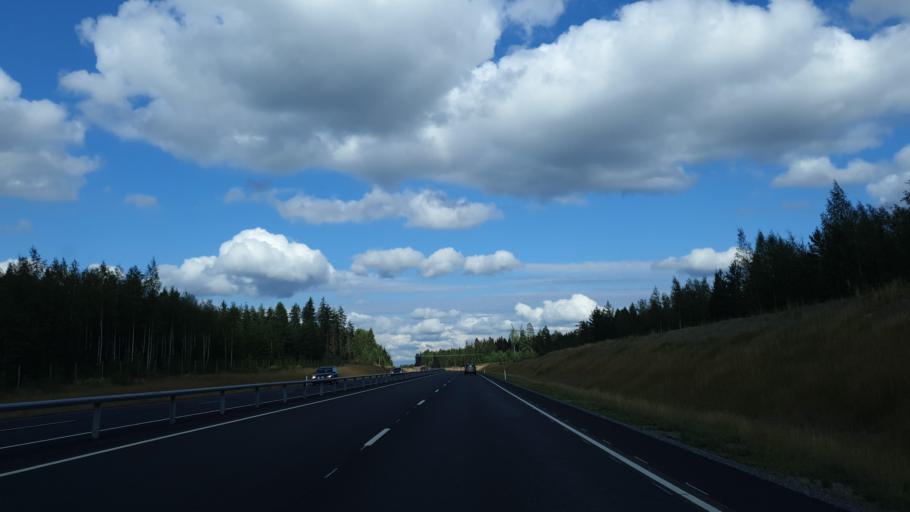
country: FI
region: Southern Savonia
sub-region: Mikkeli
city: Mikkeli
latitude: 61.7219
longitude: 27.3571
